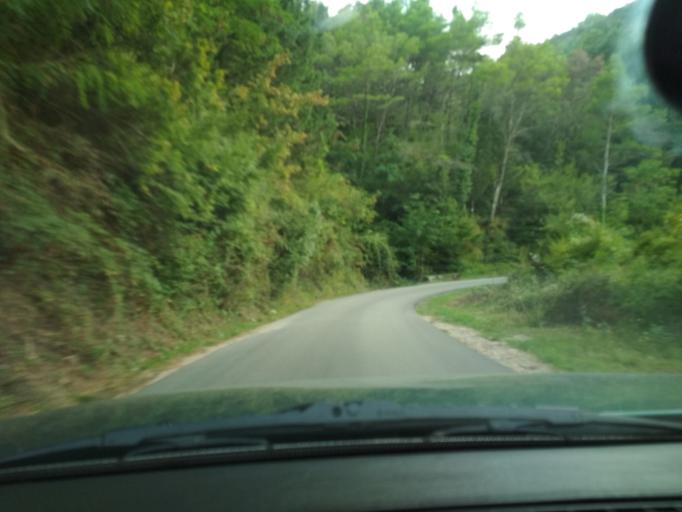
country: ME
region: Kotor
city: Kotor
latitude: 42.3972
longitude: 18.7674
